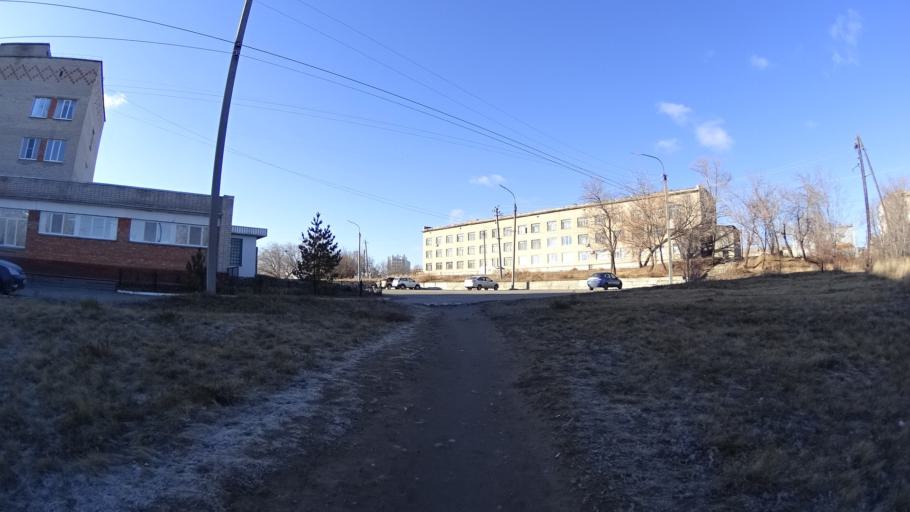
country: RU
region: Chelyabinsk
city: Troitsk
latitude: 54.0765
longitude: 61.5342
